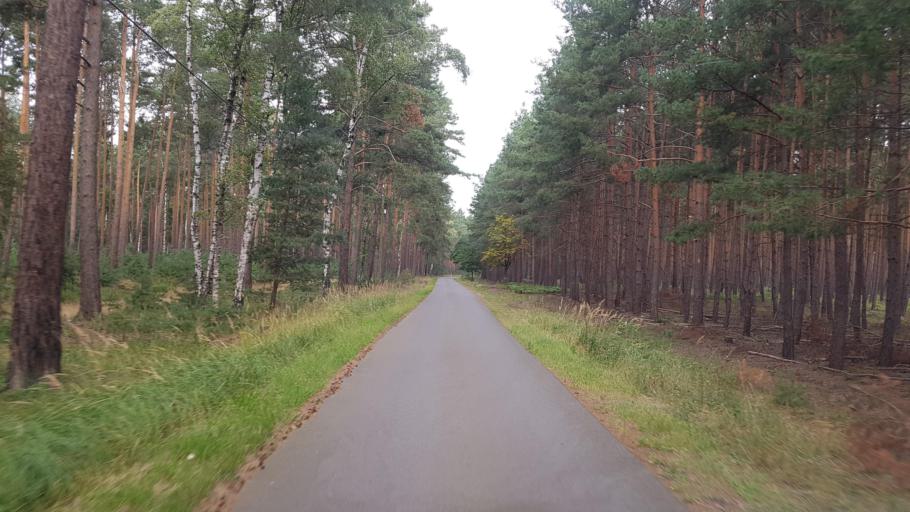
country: DE
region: Brandenburg
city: Schonewalde
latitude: 51.7837
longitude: 13.5924
